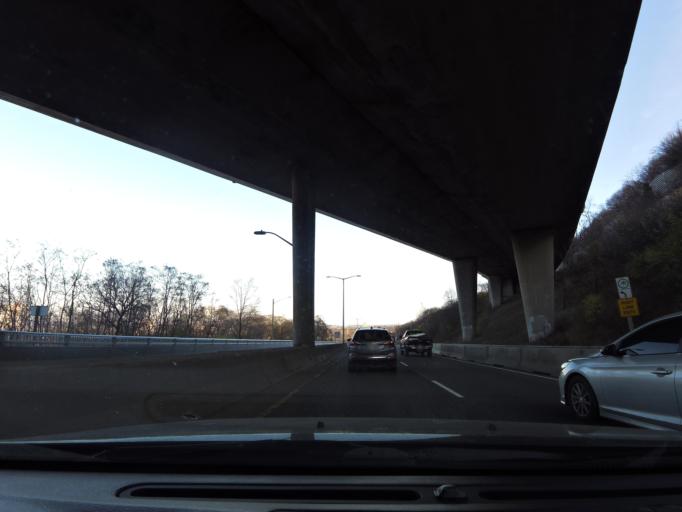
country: CA
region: Ontario
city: Hamilton
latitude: 43.2460
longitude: -79.8651
